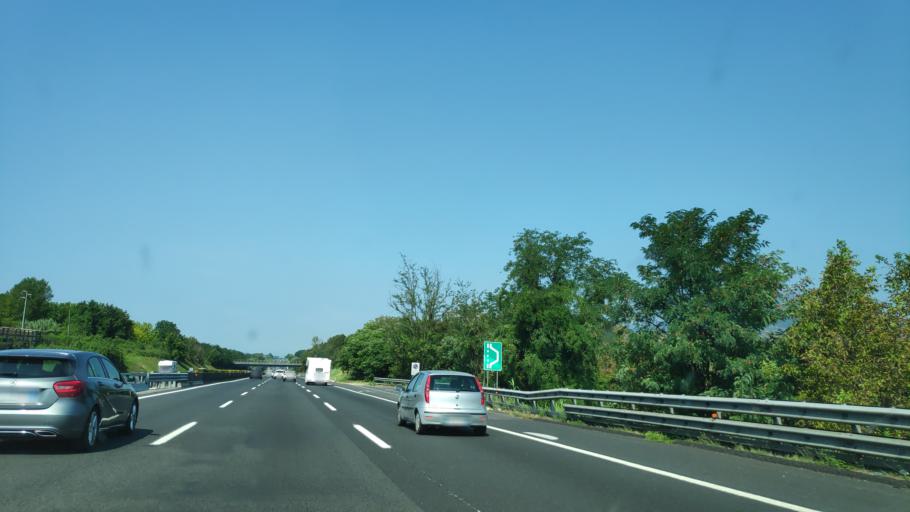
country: IT
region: Latium
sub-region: Provincia di Frosinone
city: San Bartolomeo
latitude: 41.4474
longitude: 13.8486
